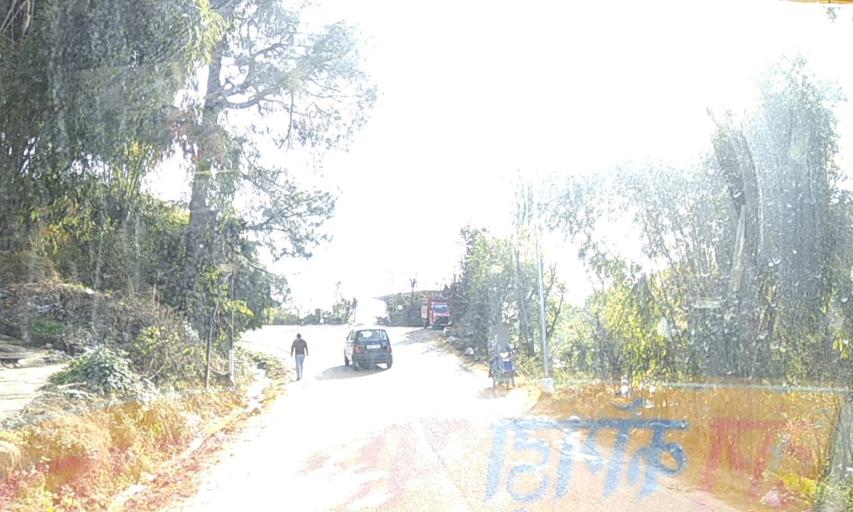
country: IN
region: Himachal Pradesh
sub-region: Kangra
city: Palampur
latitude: 32.0846
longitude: 76.5217
